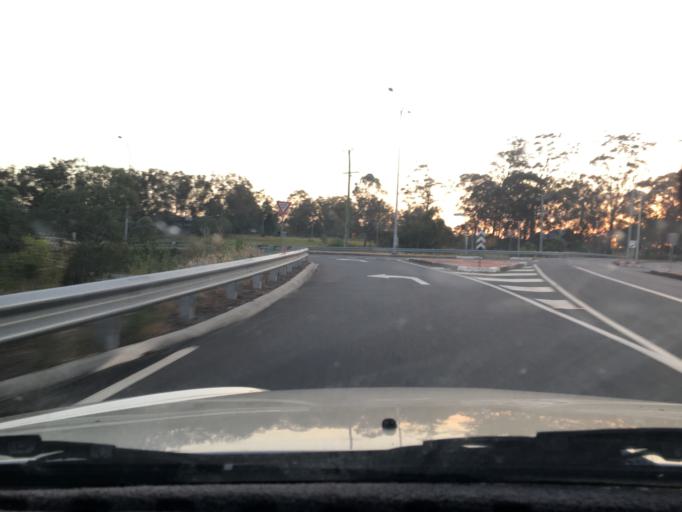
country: AU
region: Queensland
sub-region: Logan
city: Waterford West
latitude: -27.7089
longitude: 153.1454
